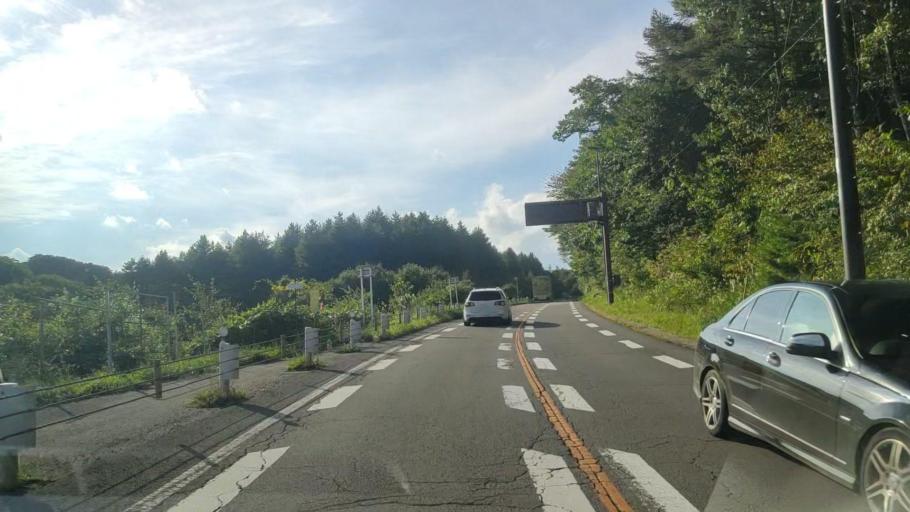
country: JP
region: Nagano
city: Ueda
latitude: 36.4855
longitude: 138.4275
